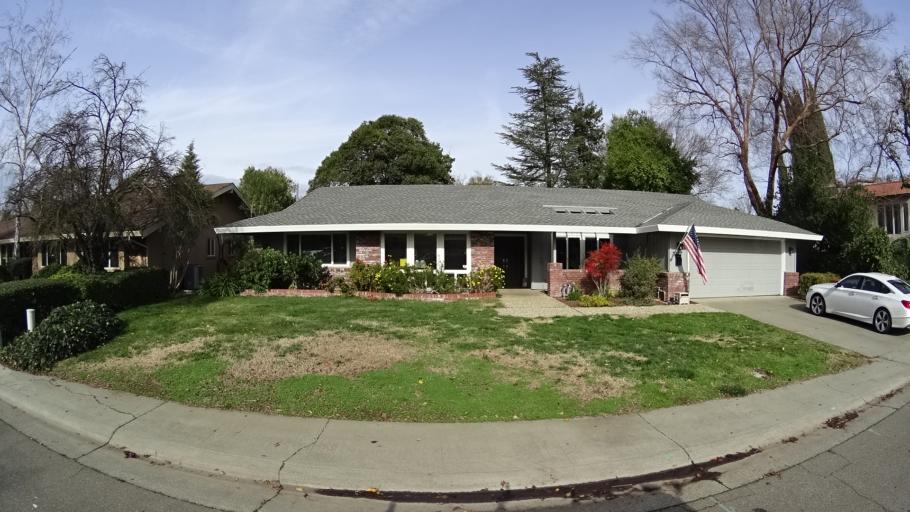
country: US
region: California
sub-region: Yolo County
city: Davis
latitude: 38.5487
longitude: -121.6885
